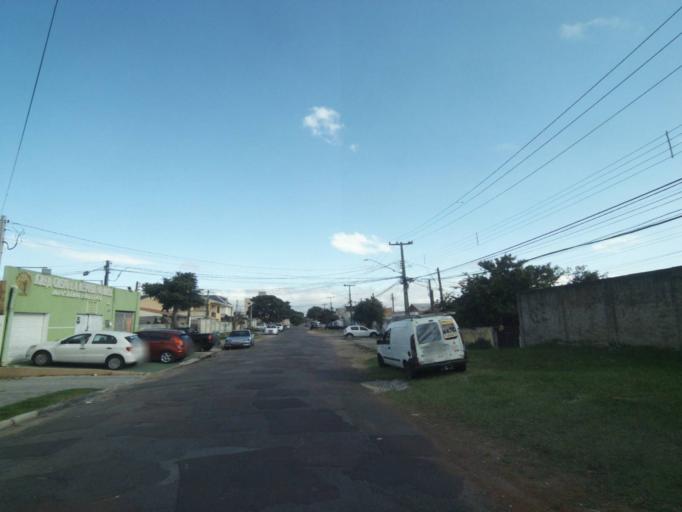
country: BR
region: Parana
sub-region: Pinhais
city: Pinhais
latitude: -25.4555
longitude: -49.2061
